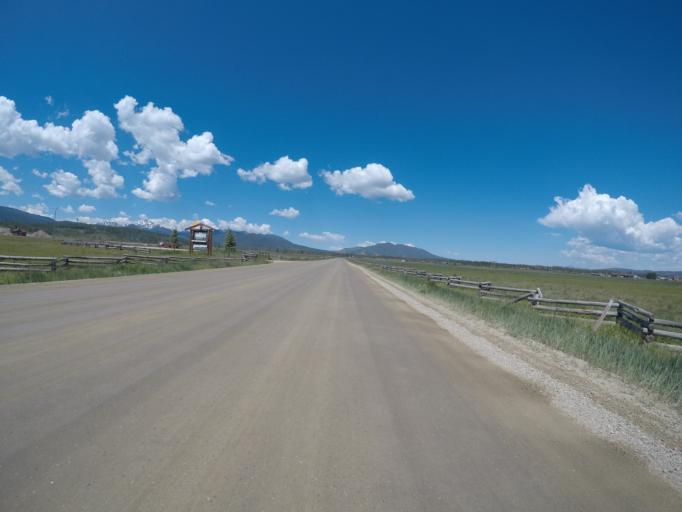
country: US
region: Colorado
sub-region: Grand County
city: Fraser
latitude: 39.9401
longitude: -105.8157
